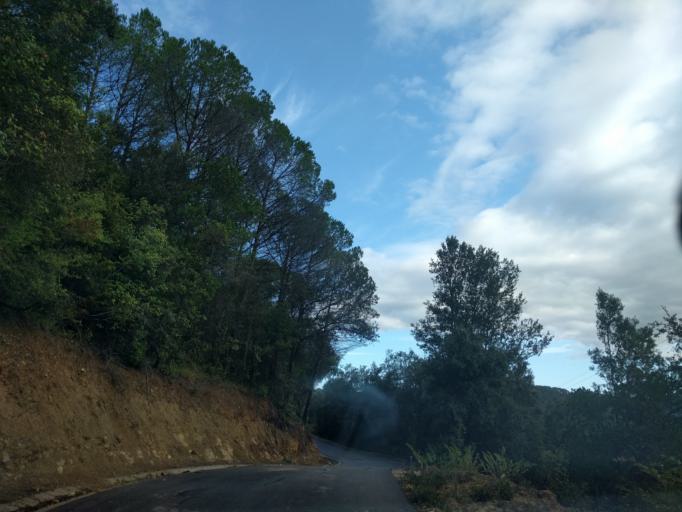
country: ES
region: Catalonia
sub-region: Provincia de Girona
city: la Cellera de Ter
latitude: 42.0335
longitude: 2.6256
